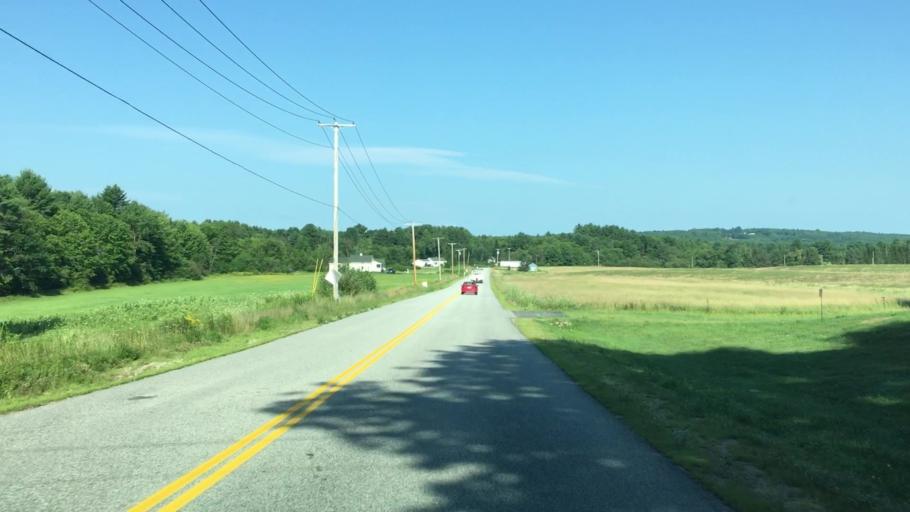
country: US
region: Maine
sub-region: Androscoggin County
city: Minot
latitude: 44.0434
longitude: -70.3237
